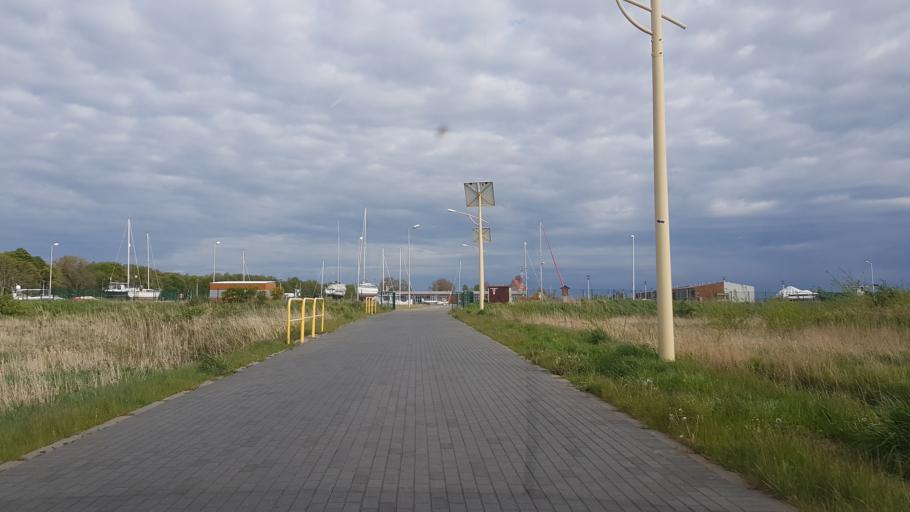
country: PL
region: West Pomeranian Voivodeship
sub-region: Powiat slawienski
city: Darlowo
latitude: 54.4349
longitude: 16.3848
